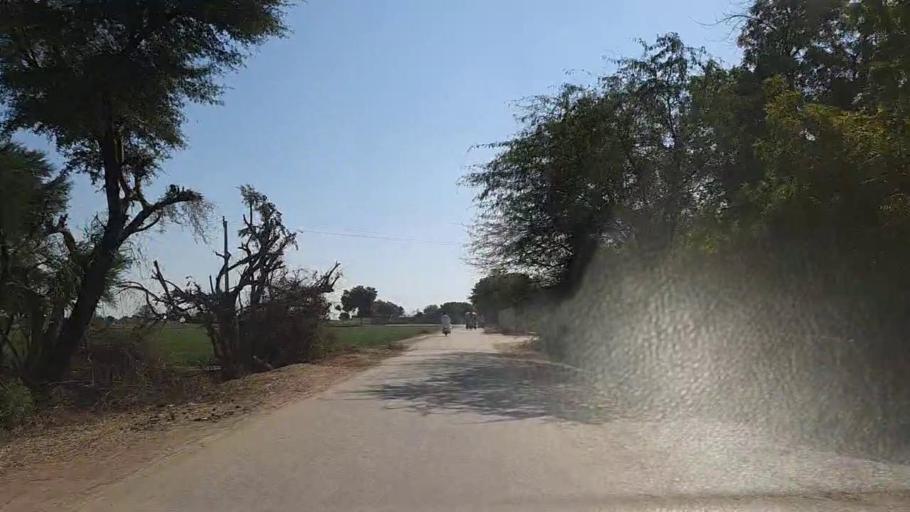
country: PK
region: Sindh
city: Nawabshah
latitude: 26.2405
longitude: 68.4457
